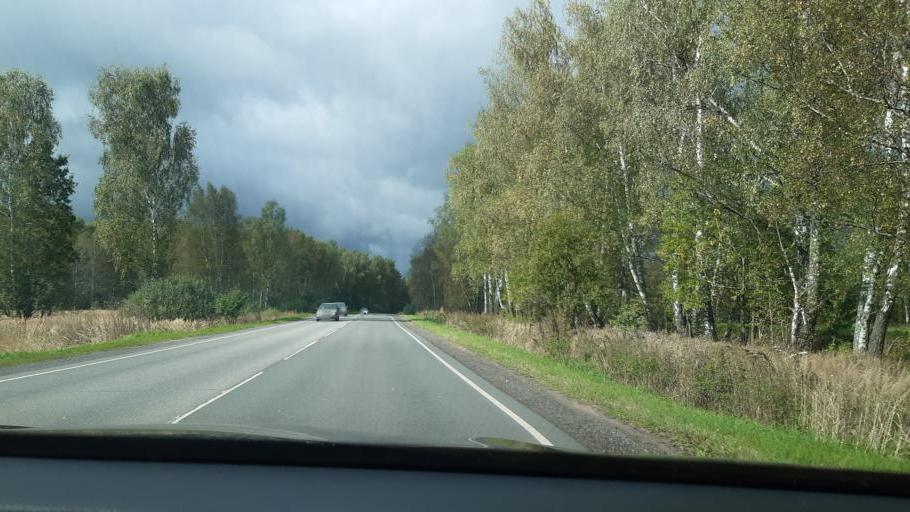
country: RU
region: Moskovskaya
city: Melikhovo
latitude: 55.1191
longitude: 37.6328
